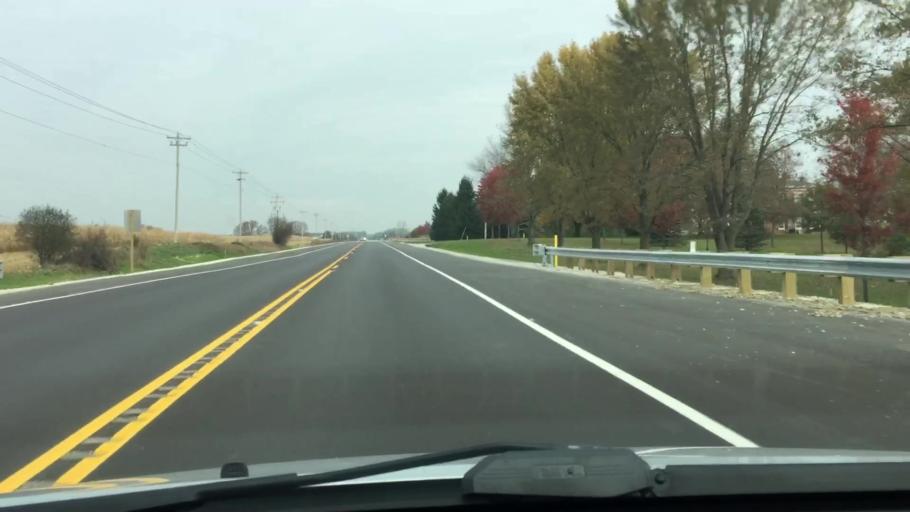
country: US
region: Wisconsin
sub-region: Waukesha County
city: Dousman
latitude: 43.0263
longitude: -88.4624
